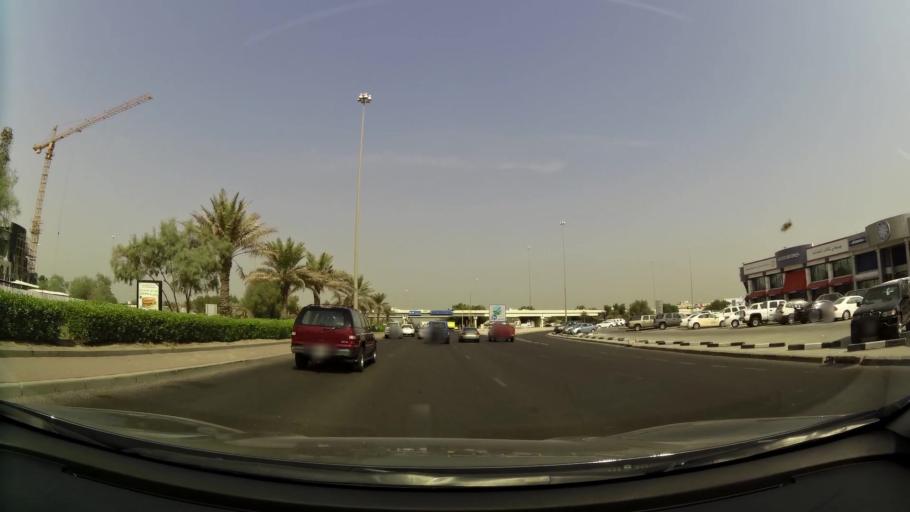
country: KW
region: Al Asimah
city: Ar Rabiyah
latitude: 29.3113
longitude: 47.9266
